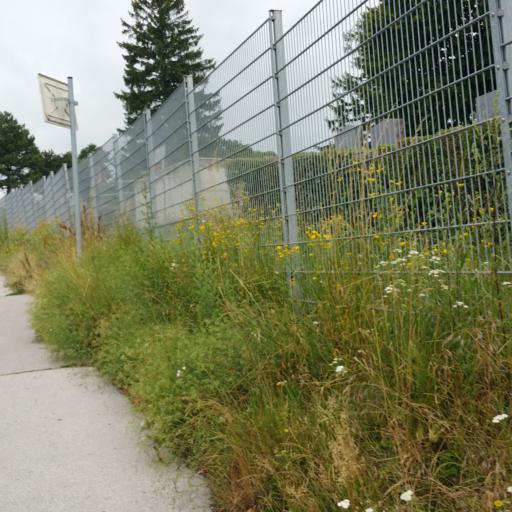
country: AT
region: Vienna
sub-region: Wien Stadt
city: Vienna
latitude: 48.2120
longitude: 16.2942
